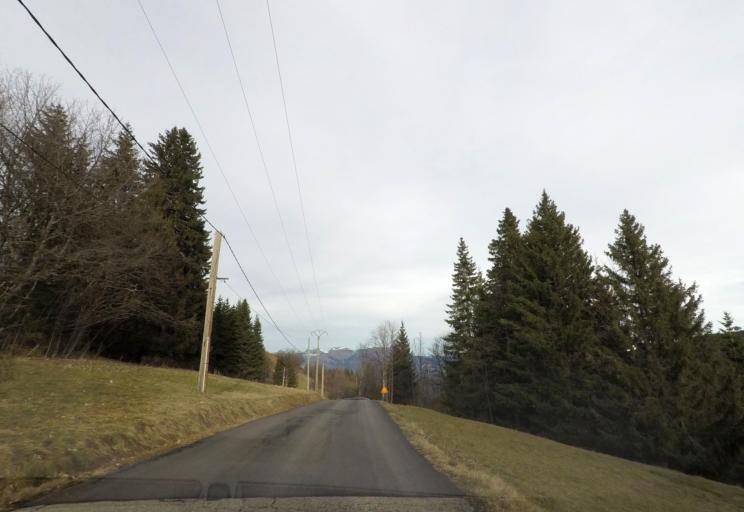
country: FR
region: Rhone-Alpes
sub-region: Departement de la Haute-Savoie
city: Ayse
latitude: 46.0339
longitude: 6.4341
